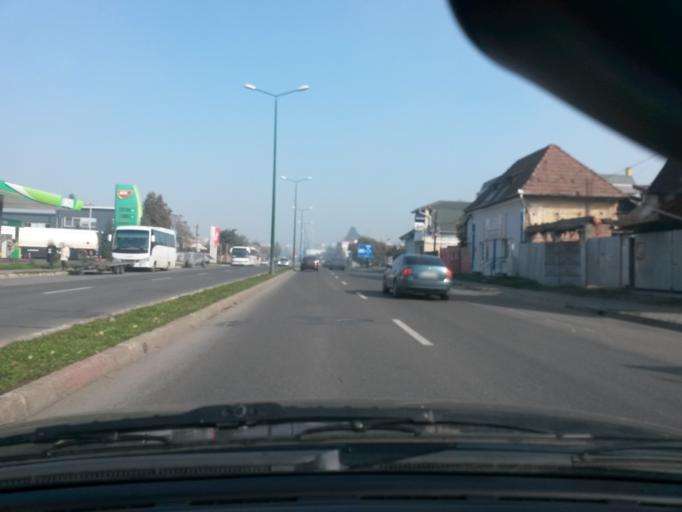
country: RO
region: Mures
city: Targu-Mures
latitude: 46.5272
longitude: 24.5428
